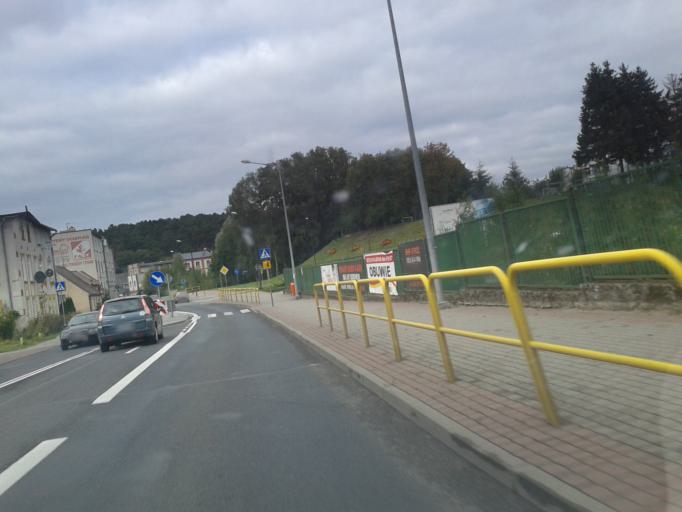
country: PL
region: Kujawsko-Pomorskie
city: Kamien Krajenski
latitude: 53.5343
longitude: 17.5220
